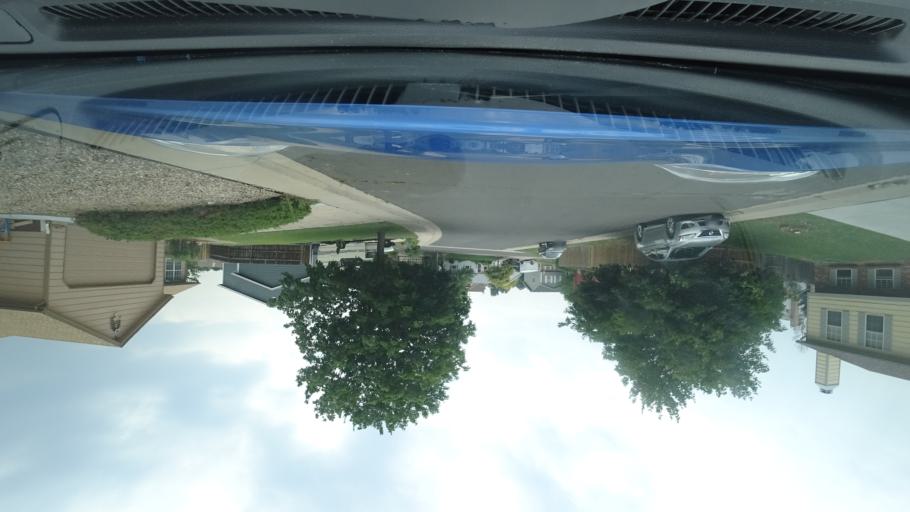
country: US
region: Colorado
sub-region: Adams County
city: Aurora
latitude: 39.6833
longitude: -104.7616
